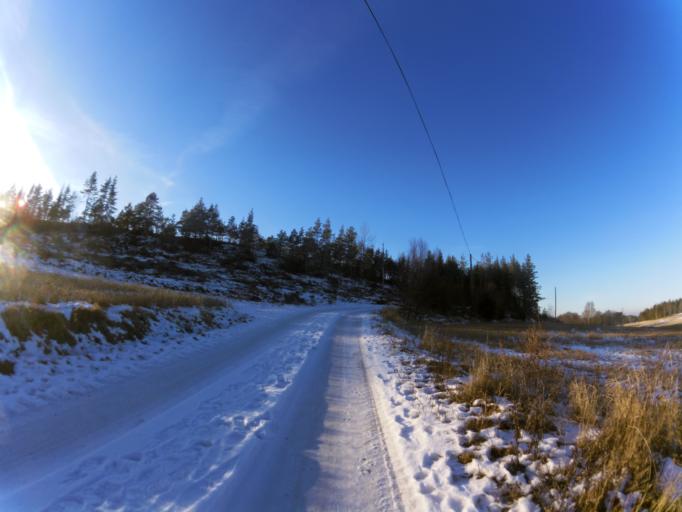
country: NO
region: Ostfold
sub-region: Fredrikstad
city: Lervik
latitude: 59.2368
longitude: 10.8230
